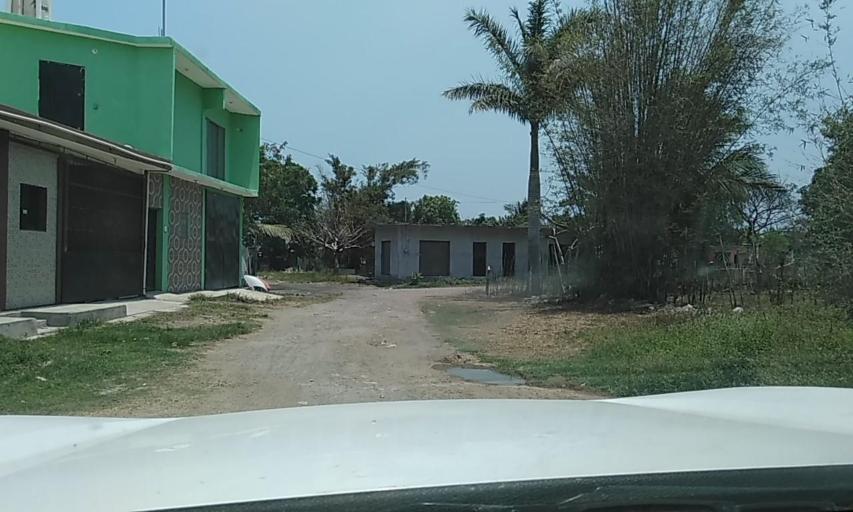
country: MX
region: Veracruz
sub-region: Veracruz
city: Las Amapolas
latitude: 19.1528
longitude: -96.2003
